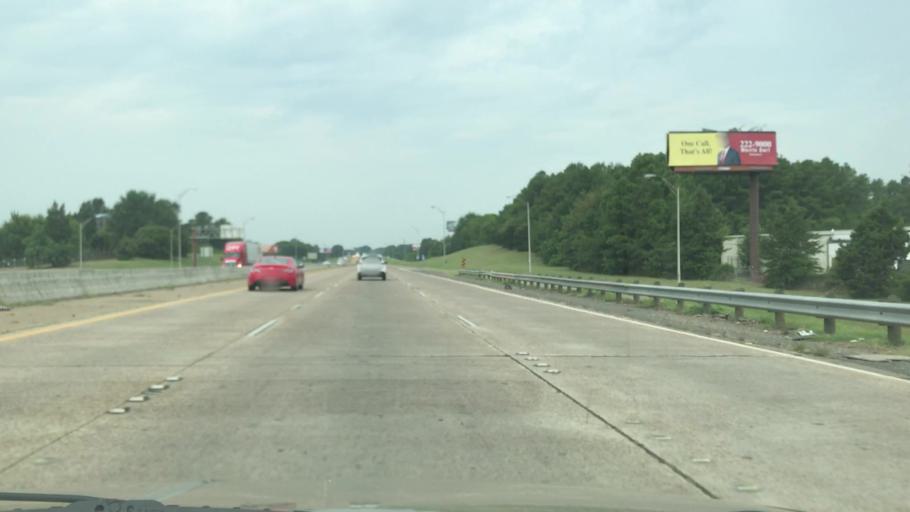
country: US
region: Louisiana
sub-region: Caddo Parish
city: Shreveport
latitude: 32.4721
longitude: -93.7981
